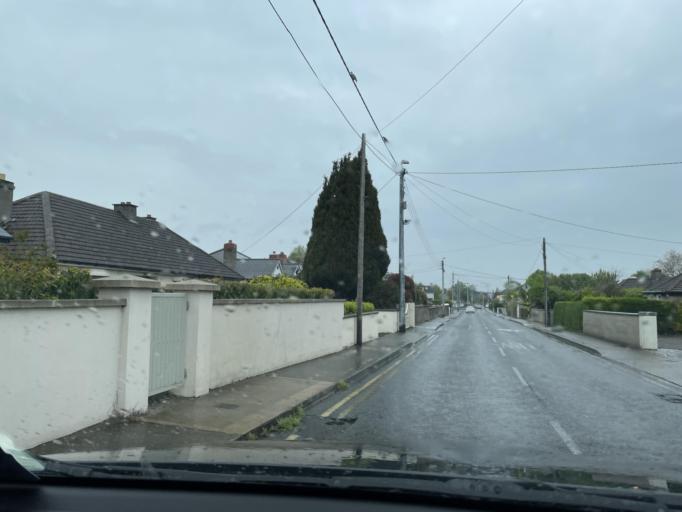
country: IE
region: Leinster
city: Dundrum
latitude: 53.2926
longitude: -6.2576
